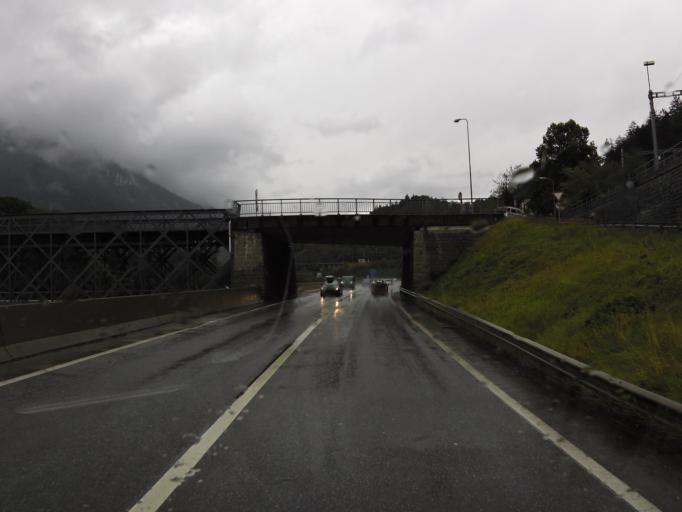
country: CH
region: Grisons
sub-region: Imboden District
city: Tamins
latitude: 46.8234
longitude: 9.4098
